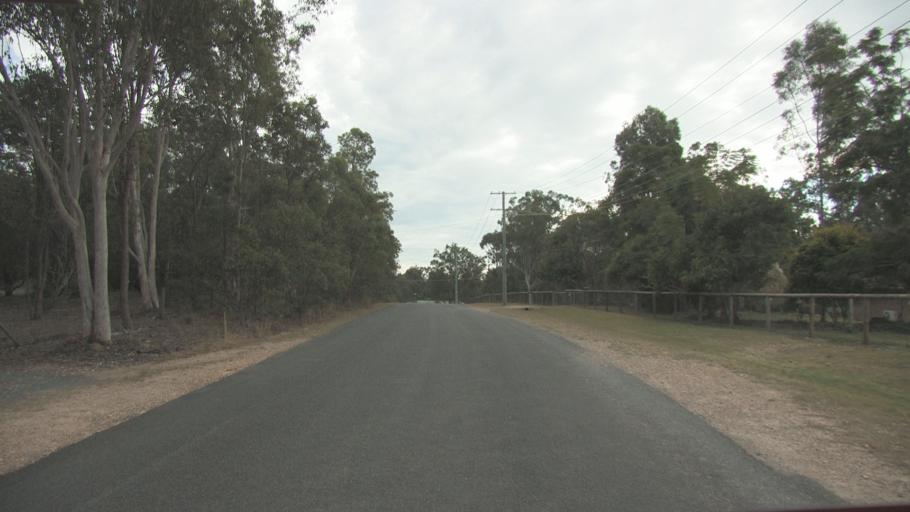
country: AU
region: Queensland
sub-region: Logan
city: Logan Reserve
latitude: -27.7443
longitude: 153.1383
